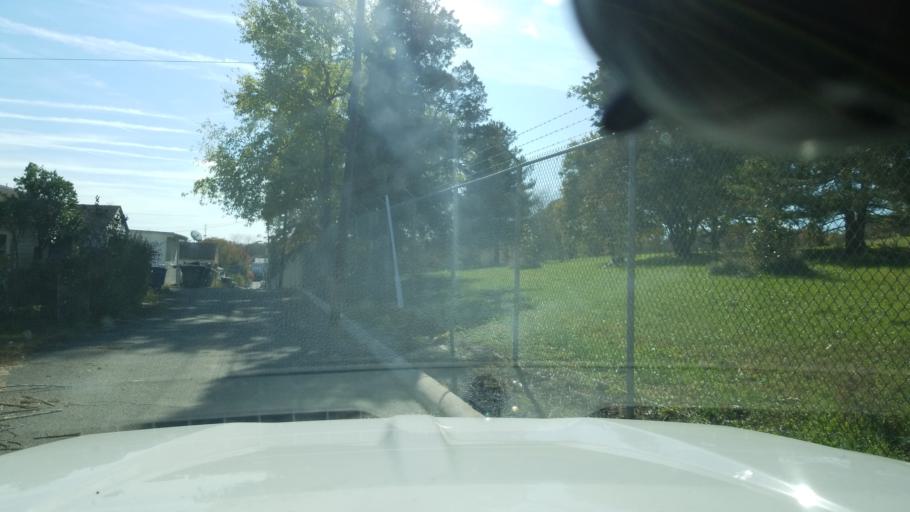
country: US
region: Maryland
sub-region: Prince George's County
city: Mount Rainier
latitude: 38.9385
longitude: -76.9821
